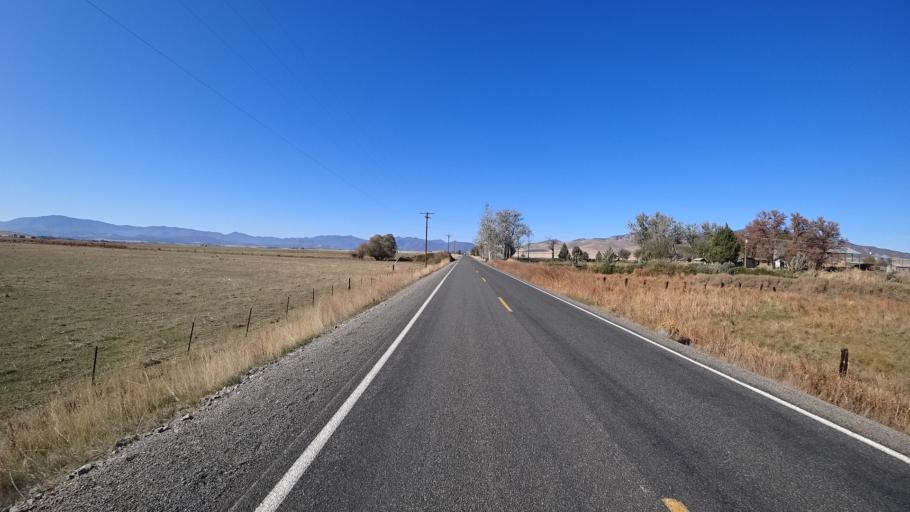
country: US
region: California
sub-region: Siskiyou County
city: Montague
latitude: 41.7706
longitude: -122.4839
